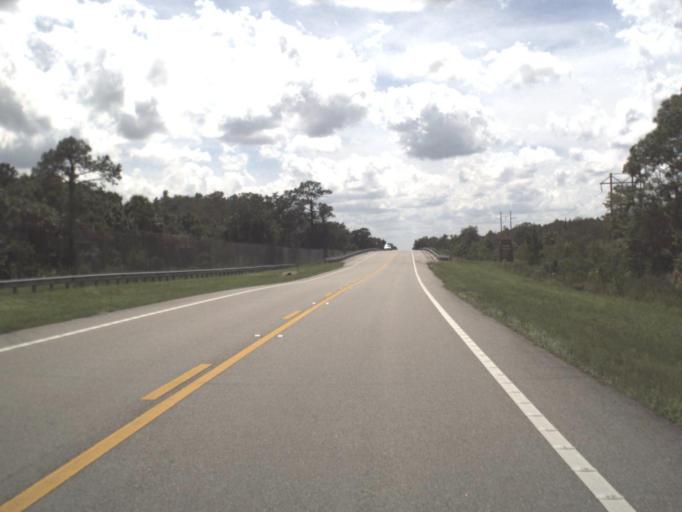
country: US
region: Florida
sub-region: Collier County
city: Immokalee
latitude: 26.2495
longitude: -81.3418
